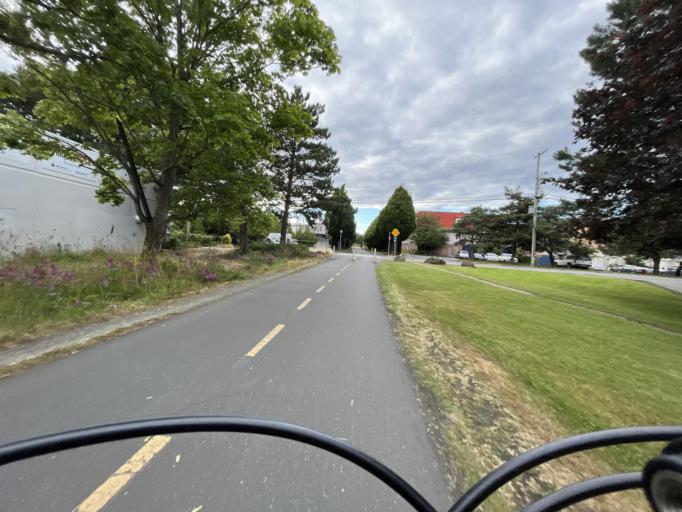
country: CA
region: British Columbia
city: Victoria
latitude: 48.4505
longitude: -123.3755
